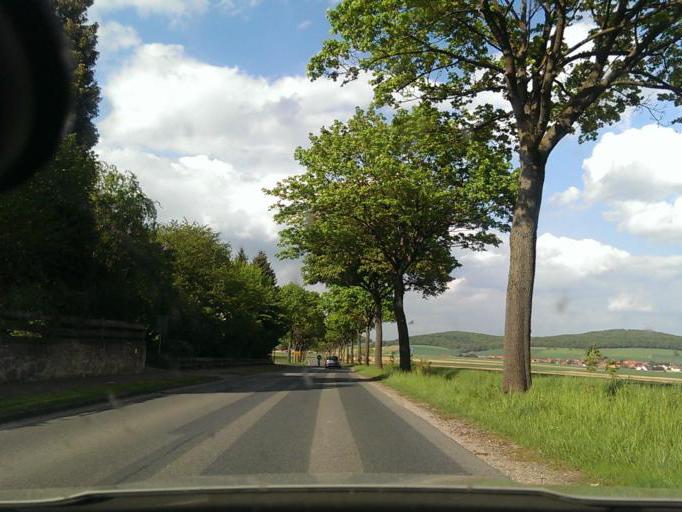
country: DE
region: Lower Saxony
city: Marienhagen
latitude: 52.0391
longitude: 9.6906
